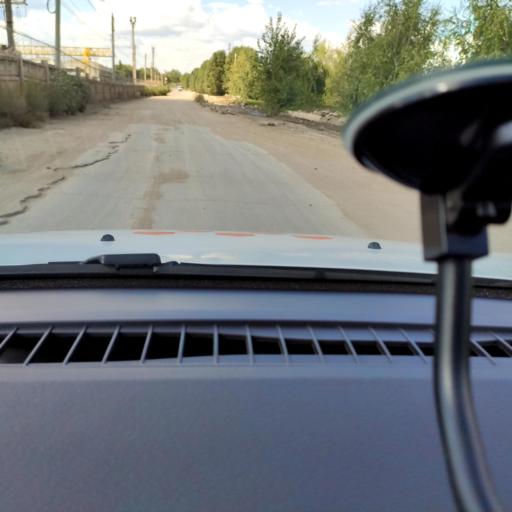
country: RU
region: Samara
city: Samara
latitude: 53.1825
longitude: 50.2629
